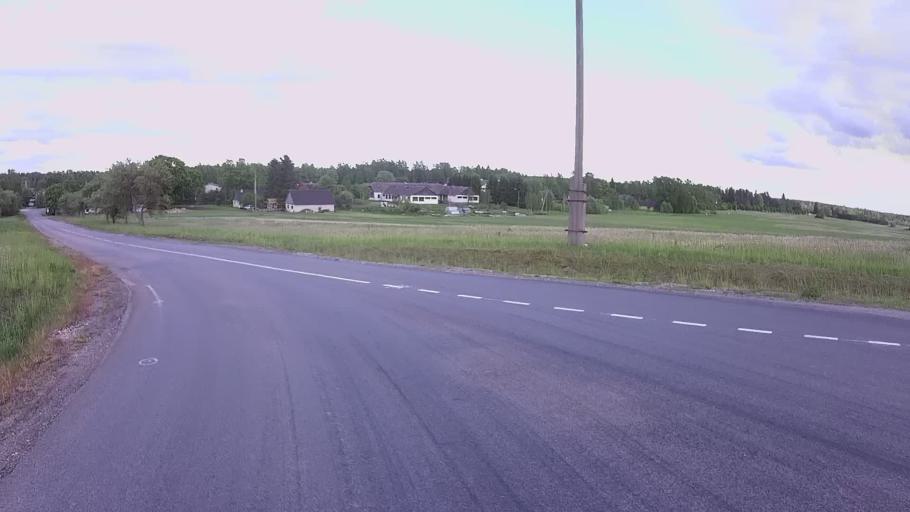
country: EE
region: Jogevamaa
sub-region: Mustvee linn
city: Mustvee
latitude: 59.0370
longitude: 27.0777
